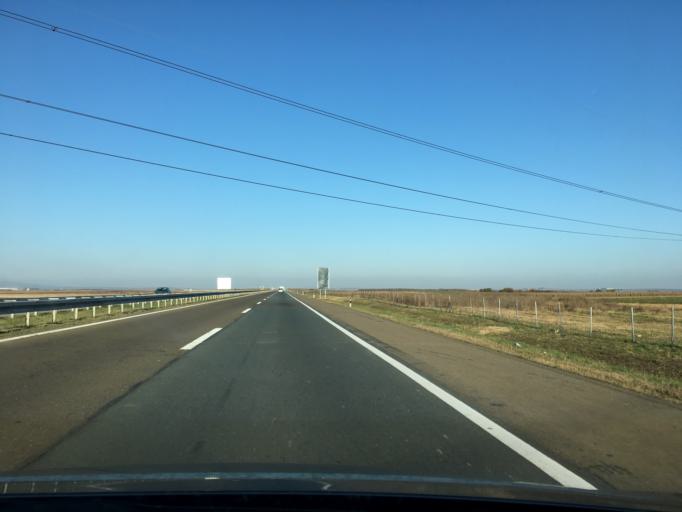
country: RS
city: Novi Karlovci
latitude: 45.0769
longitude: 20.1430
